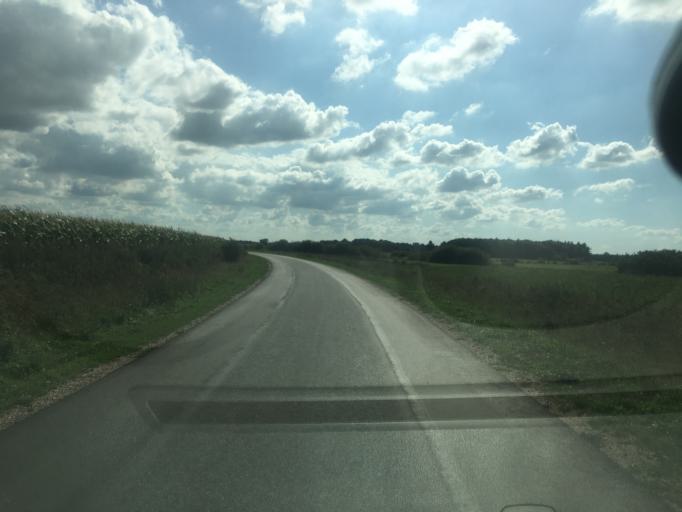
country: DK
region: South Denmark
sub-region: Tonder Kommune
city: Logumkloster
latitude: 54.9961
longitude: 9.0125
